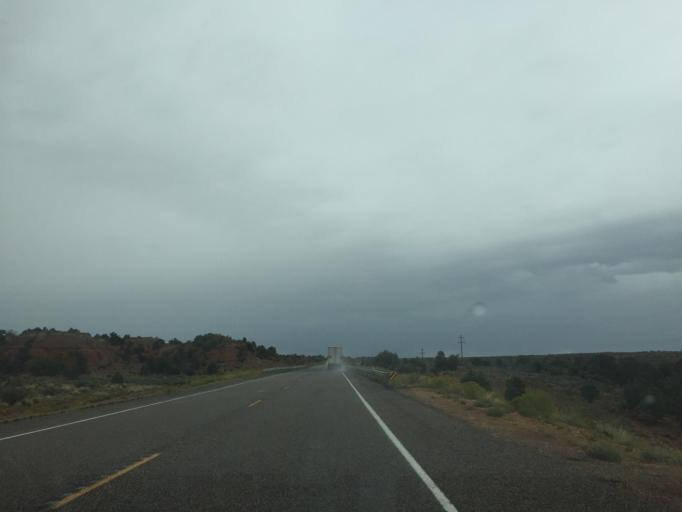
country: US
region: Utah
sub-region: Kane County
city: Kanab
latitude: 37.0627
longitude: -112.1866
